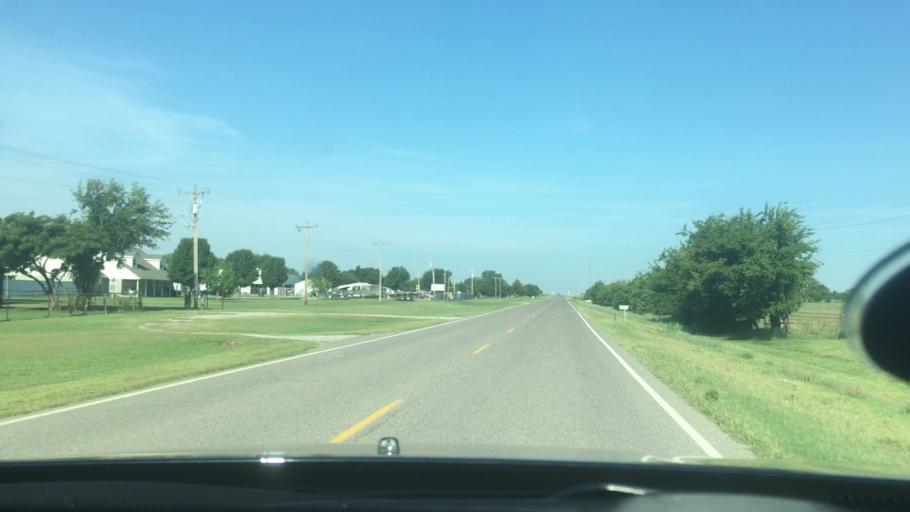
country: US
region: Oklahoma
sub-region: Garvin County
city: Wynnewood
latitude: 34.6518
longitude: -97.2360
